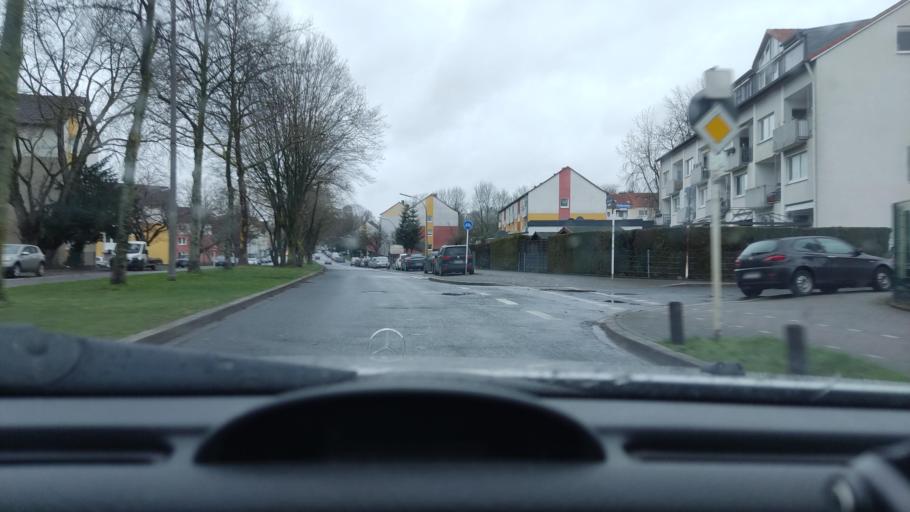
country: DE
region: North Rhine-Westphalia
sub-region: Regierungsbezirk Arnsberg
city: Dortmund
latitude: 51.5505
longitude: 7.4909
